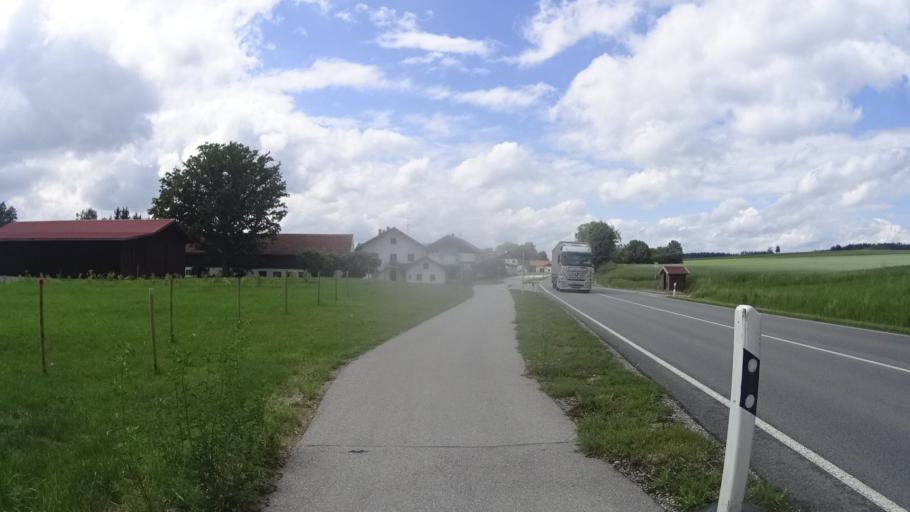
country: DE
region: Bavaria
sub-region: Lower Bavaria
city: Massing
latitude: 48.3968
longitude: 12.6338
